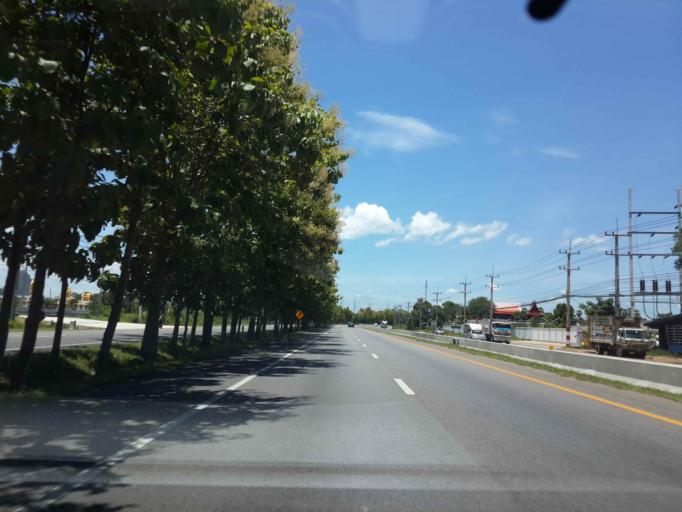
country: TH
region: Phetchaburi
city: Khao Yoi
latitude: 13.2708
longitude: 99.8209
